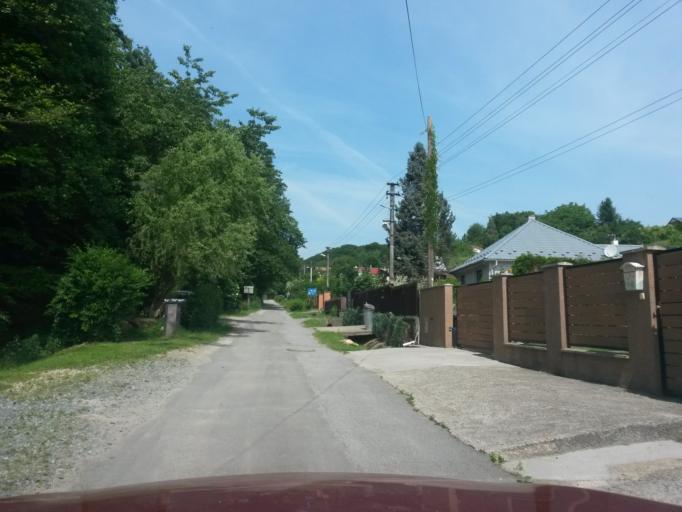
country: SK
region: Kosicky
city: Kosice
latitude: 48.7304
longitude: 21.1321
